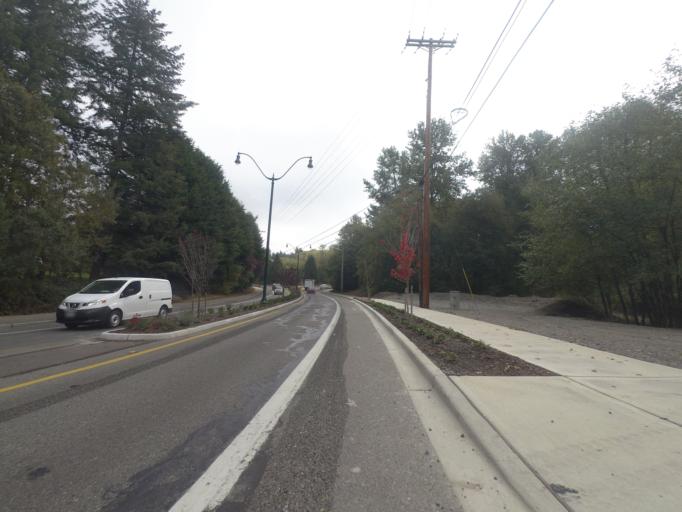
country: US
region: Washington
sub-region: Pierce County
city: Fircrest
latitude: 47.2067
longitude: -122.5178
